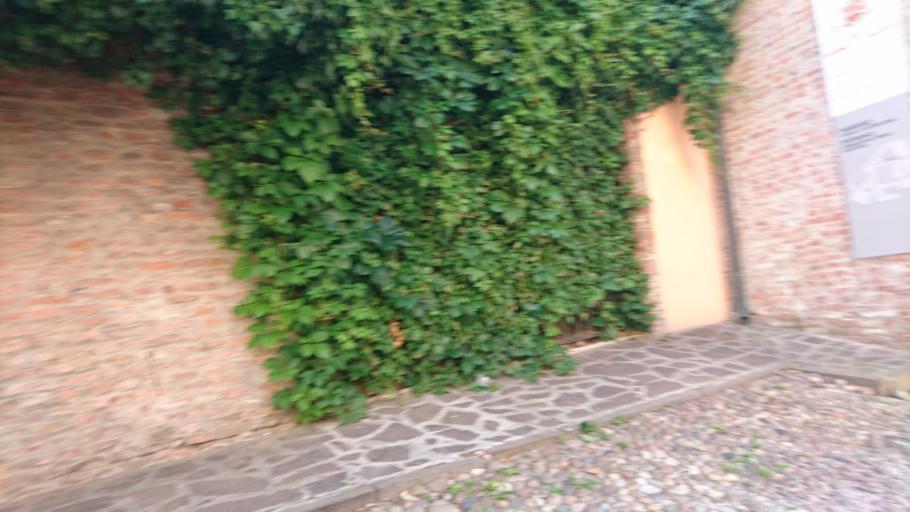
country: IT
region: Lombardy
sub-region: Provincia di Mantova
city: Mantova
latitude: 45.1589
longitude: 10.7993
